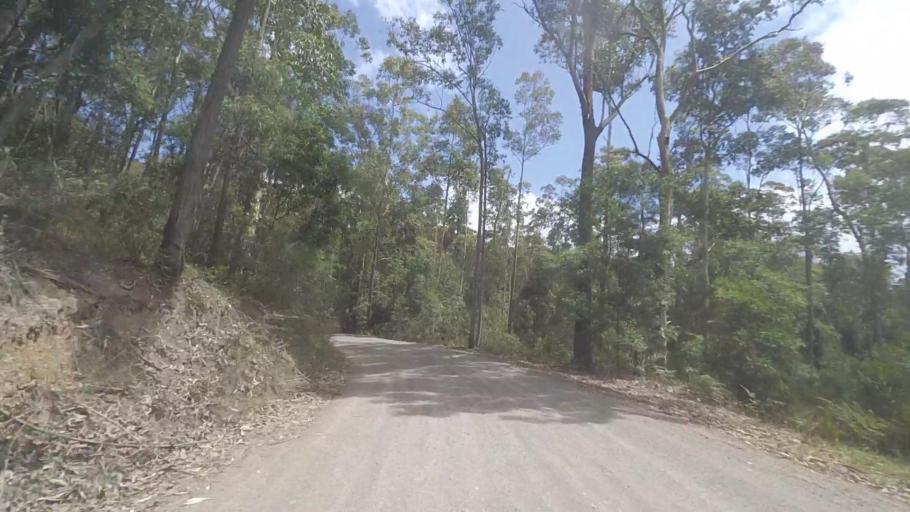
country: AU
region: New South Wales
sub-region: Shoalhaven Shire
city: Milton
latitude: -35.4391
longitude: 150.3209
